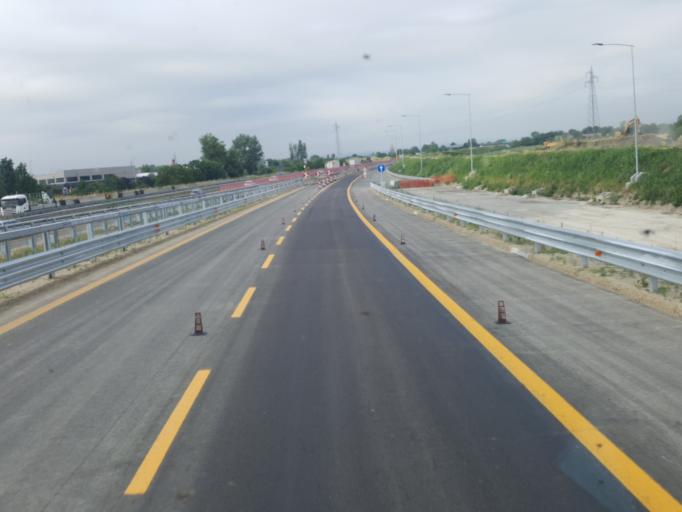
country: IT
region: Emilia-Romagna
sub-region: Provincia di Parma
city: Ponte Taro
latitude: 44.8545
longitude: 10.2302
